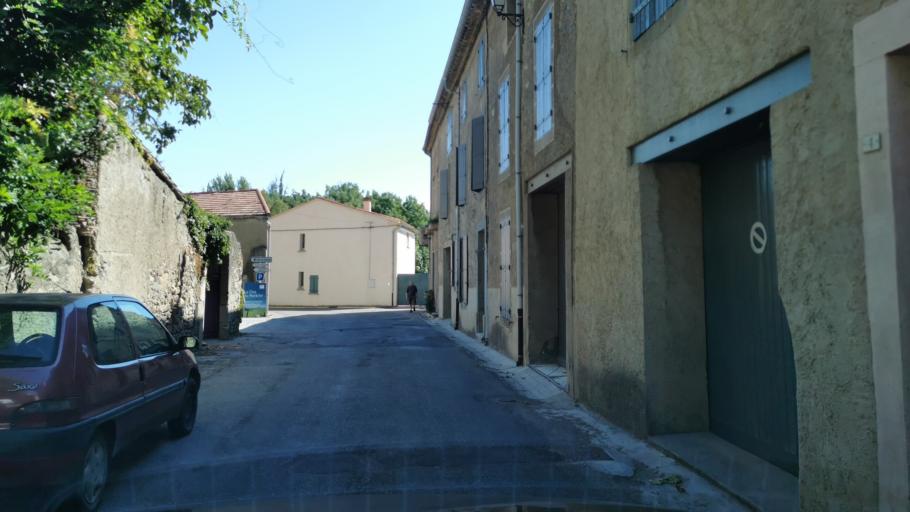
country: FR
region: Languedoc-Roussillon
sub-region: Departement de l'Aude
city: Caunes-Minervois
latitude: 43.3262
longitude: 2.5261
